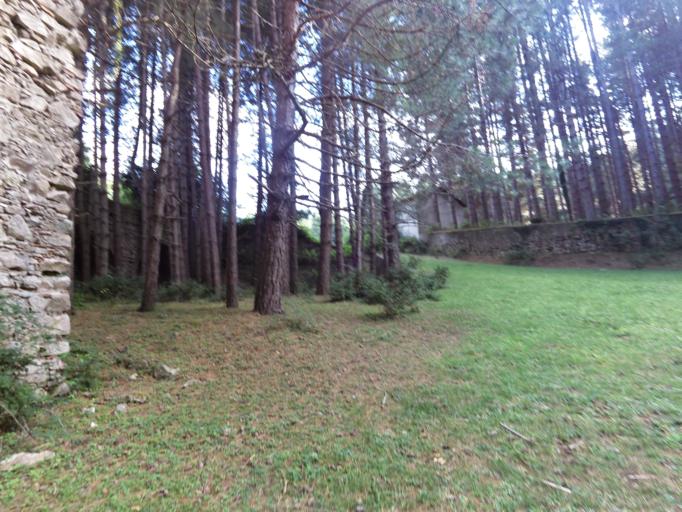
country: IT
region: Calabria
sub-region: Provincia di Vibo-Valentia
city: Nardodipace
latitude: 38.5090
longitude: 16.3789
